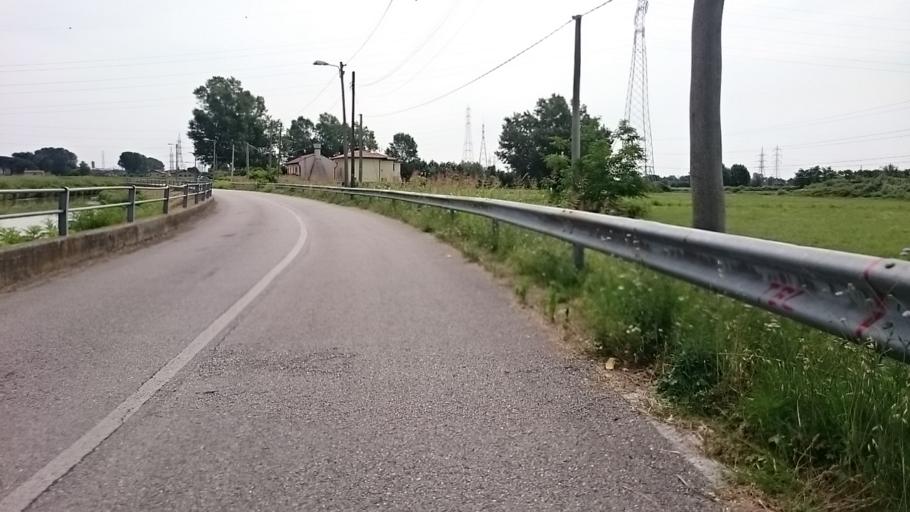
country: IT
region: Veneto
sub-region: Provincia di Venezia
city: Fornase
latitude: 45.4567
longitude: 12.1954
